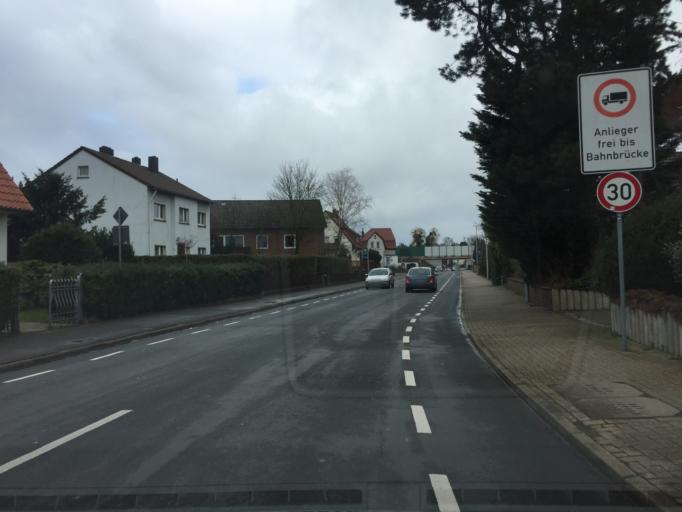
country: DE
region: Lower Saxony
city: Wunstorf
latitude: 52.4184
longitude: 9.4312
